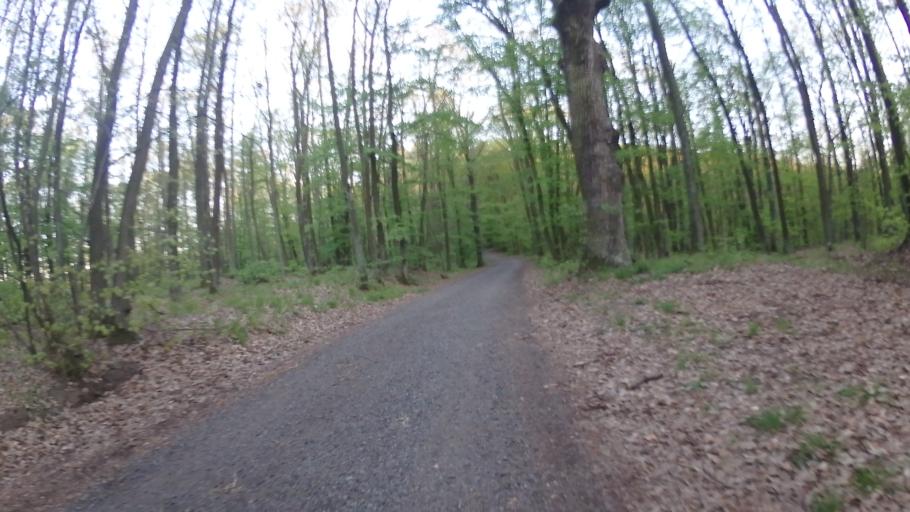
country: CZ
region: South Moravian
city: Troubsko
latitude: 49.1938
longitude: 16.5141
